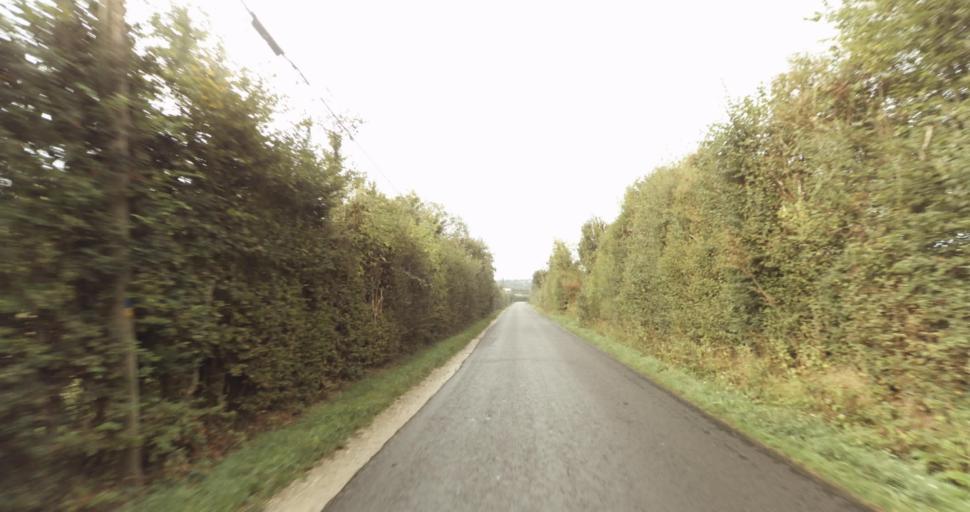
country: FR
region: Lower Normandy
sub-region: Departement de l'Orne
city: Vimoutiers
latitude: 48.9087
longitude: 0.1959
